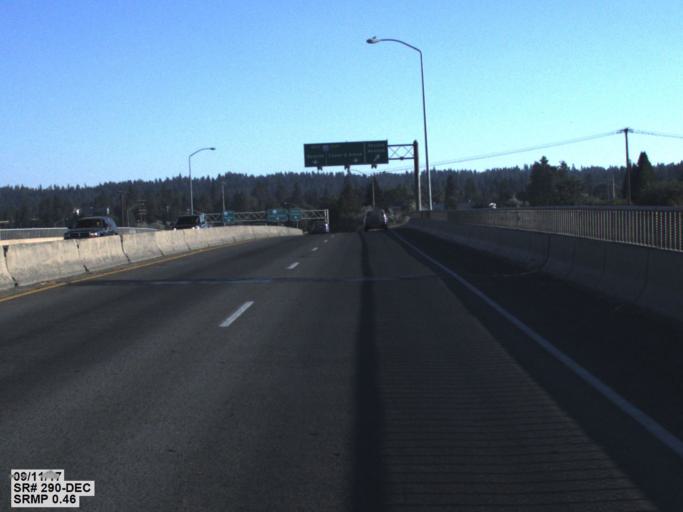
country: US
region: Washington
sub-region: Spokane County
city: Spokane
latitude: 47.6579
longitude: -117.3952
